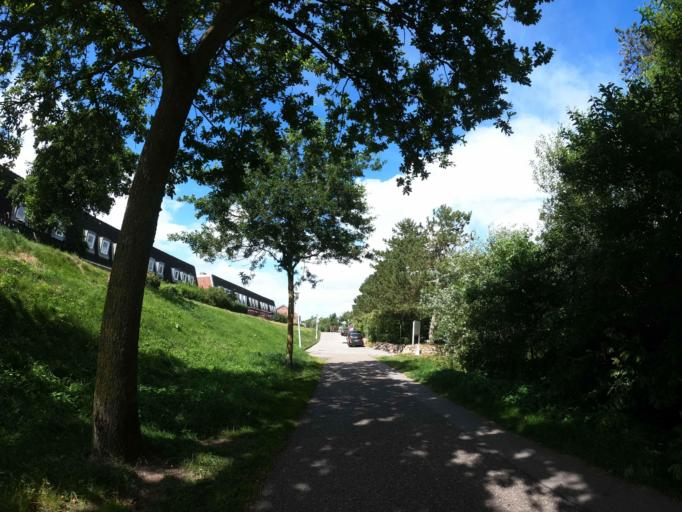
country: DE
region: Schleswig-Holstein
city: Westerland
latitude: 54.8997
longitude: 8.3137
